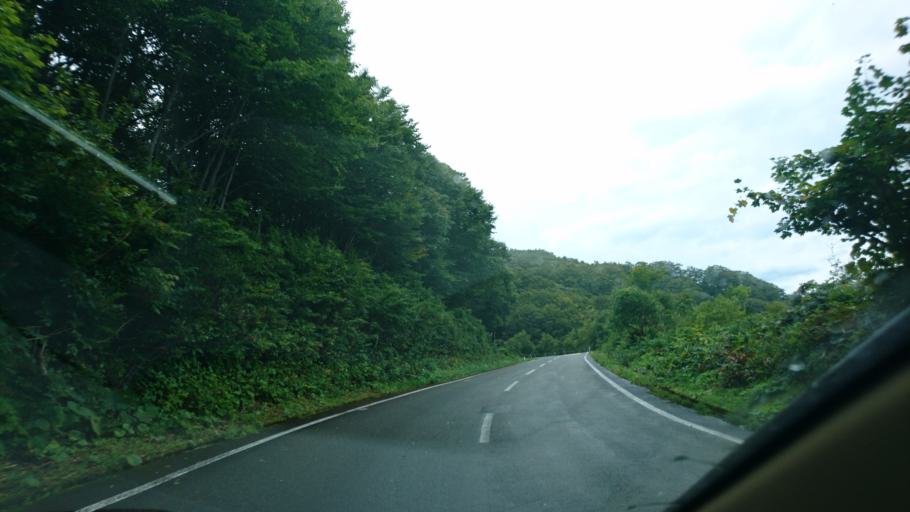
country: JP
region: Akita
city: Yuzawa
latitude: 39.1519
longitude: 140.7549
